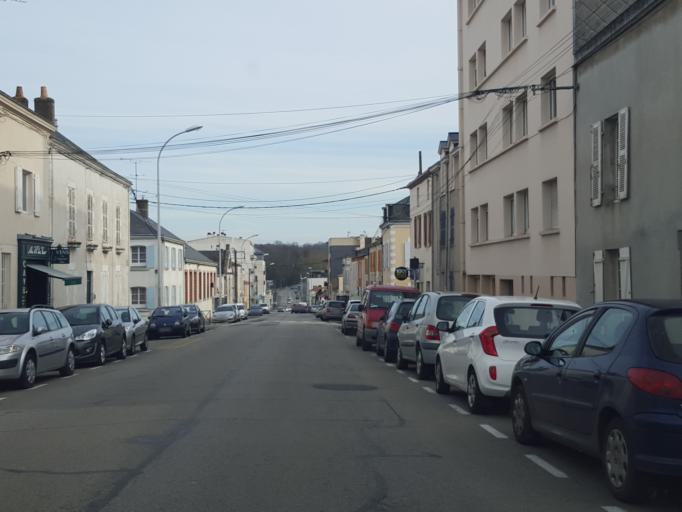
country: FR
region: Pays de la Loire
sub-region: Departement de la Vendee
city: La Roche-sur-Yon
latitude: 46.6714
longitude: -1.4211
